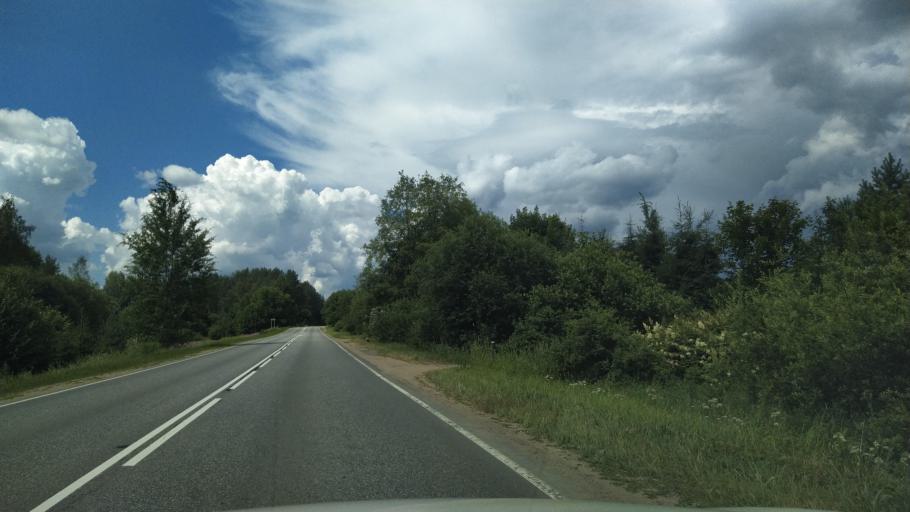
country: RU
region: Leningrad
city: Rozhdestveno
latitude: 59.3445
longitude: 29.9462
